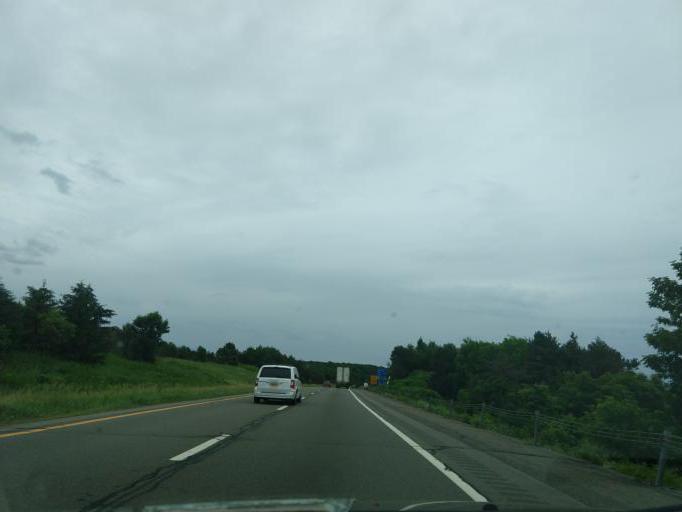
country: US
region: New York
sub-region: Chenango County
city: Lakeview
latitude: 42.3822
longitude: -75.9958
